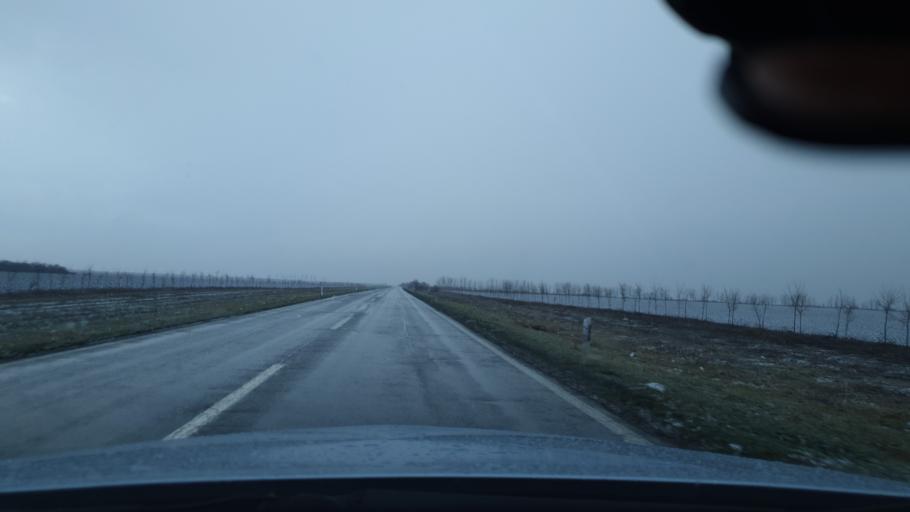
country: RS
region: Autonomna Pokrajina Vojvodina
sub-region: Juznobanatski Okrug
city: Pancevo
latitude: 44.8564
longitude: 20.7549
